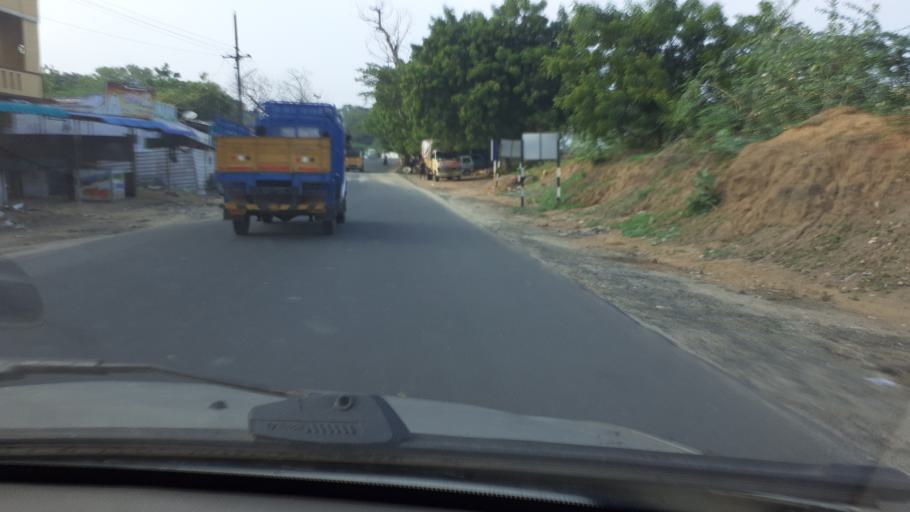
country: IN
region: Tamil Nadu
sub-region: Thoothukkudi
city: Srivaikuntam
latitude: 8.6234
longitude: 77.9096
